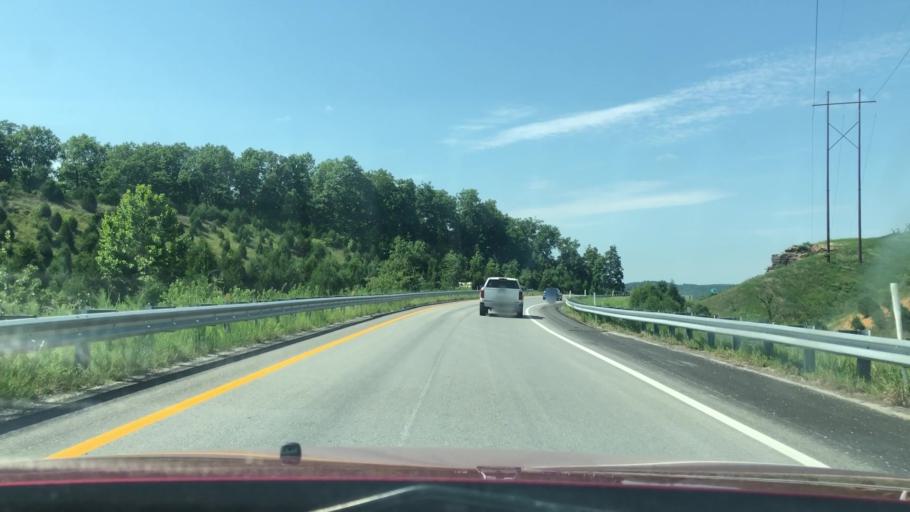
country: US
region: Missouri
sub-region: Taney County
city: Branson
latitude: 36.6777
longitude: -93.3159
